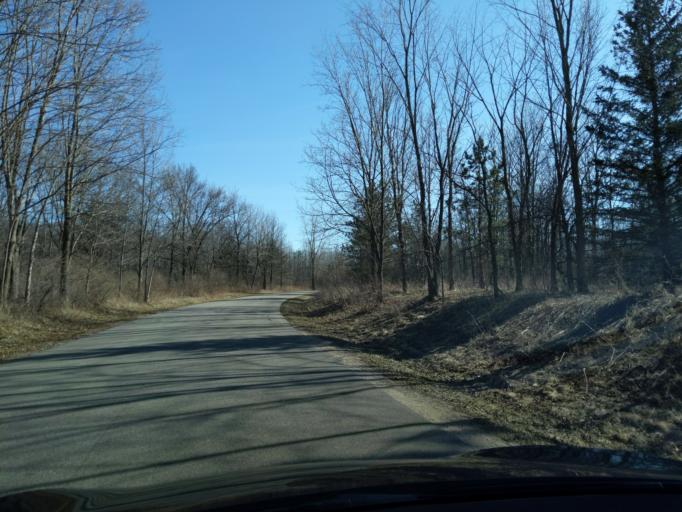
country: US
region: Michigan
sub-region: Ionia County
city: Saranac
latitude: 42.9359
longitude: -85.1346
